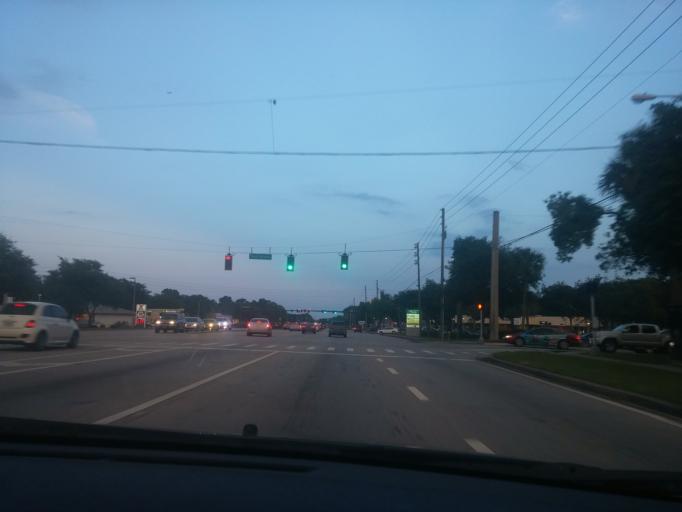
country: US
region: Florida
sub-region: Seminole County
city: Goldenrod
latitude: 28.6475
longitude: -81.2703
